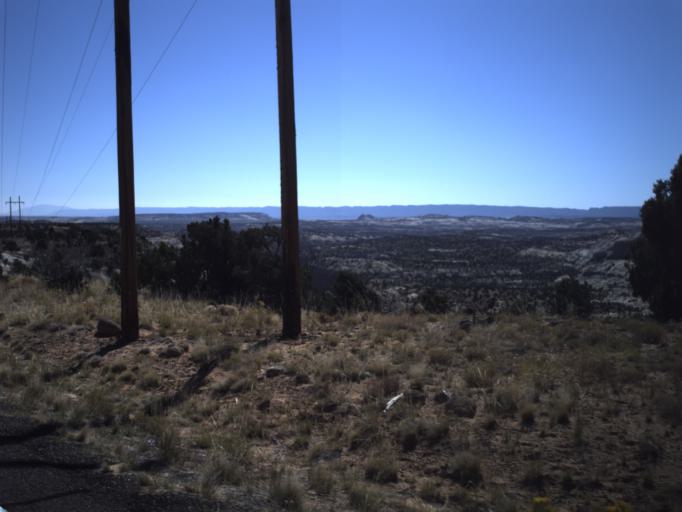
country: US
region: Utah
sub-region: Wayne County
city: Loa
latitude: 37.8432
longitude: -111.4236
